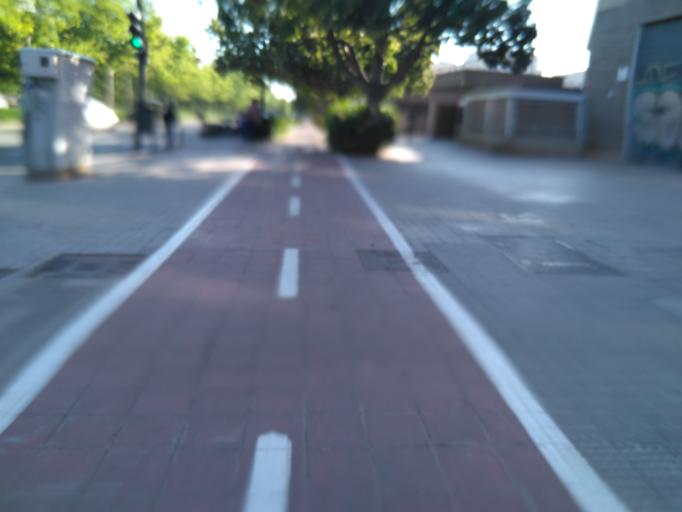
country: ES
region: Valencia
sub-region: Provincia de Valencia
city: Tavernes Blanques
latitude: 39.4920
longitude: -0.3620
